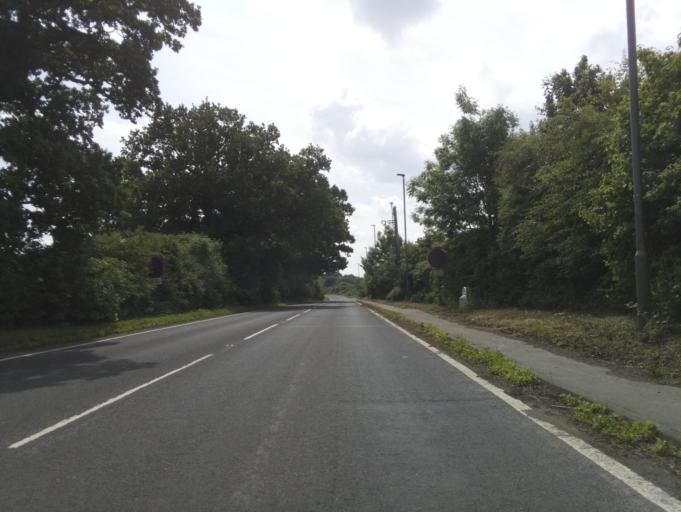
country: GB
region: England
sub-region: North Yorkshire
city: Boroughbridge
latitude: 54.0819
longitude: -1.3950
